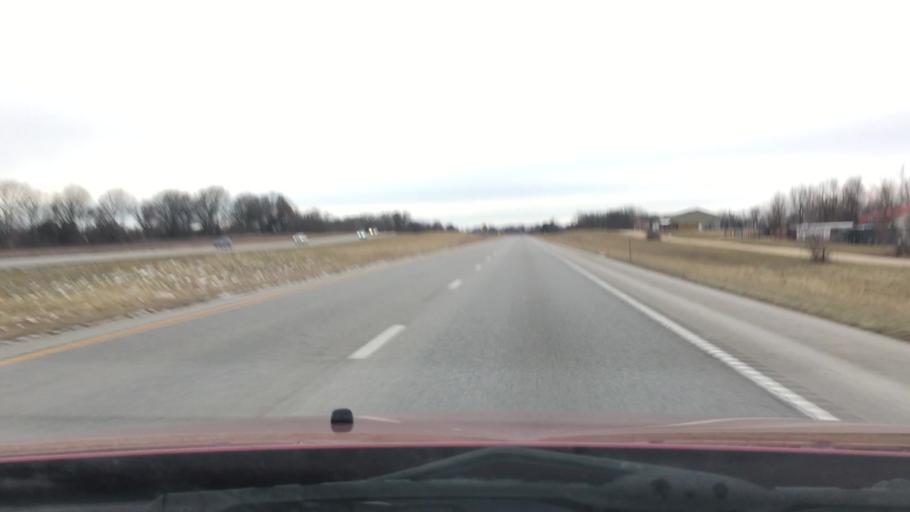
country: US
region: Missouri
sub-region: Webster County
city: Seymour
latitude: 37.1602
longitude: -92.7931
